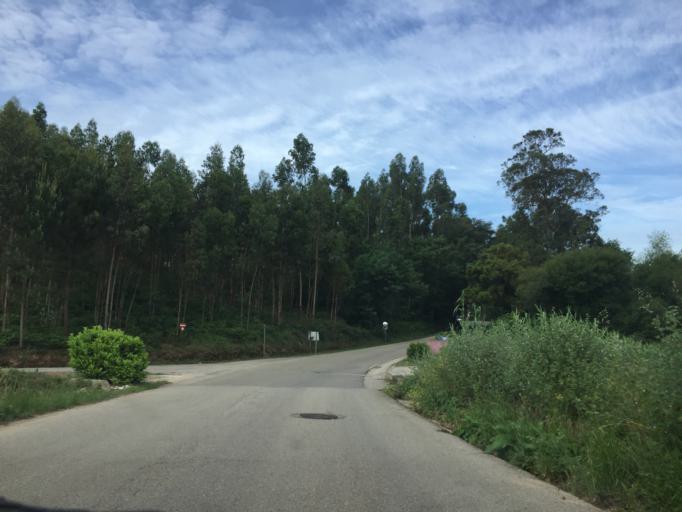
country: PT
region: Aveiro
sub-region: Anadia
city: Arcos
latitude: 40.4684
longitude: -8.4353
